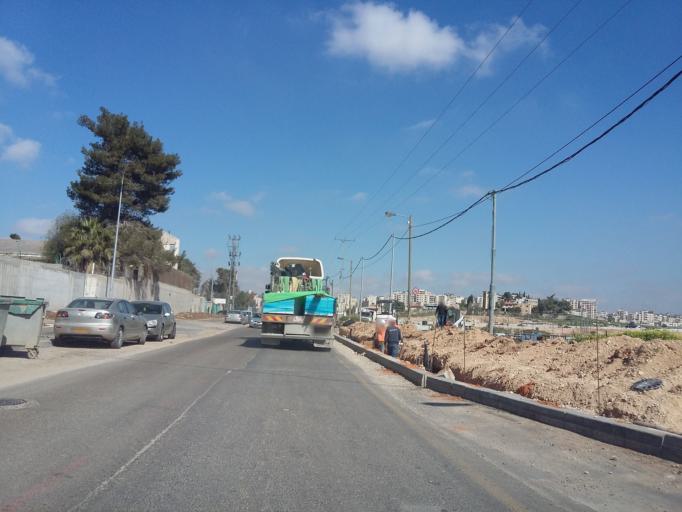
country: PS
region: West Bank
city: Ar Ram wa Dahiyat al Barid
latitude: 31.8572
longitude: 35.2228
